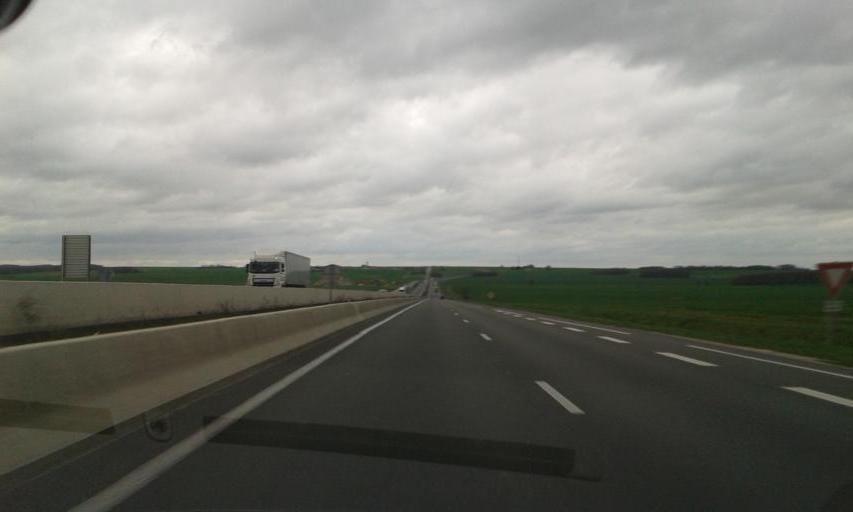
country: FR
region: Centre
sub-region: Departement d'Eure-et-Loir
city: Leves
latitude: 48.5098
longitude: 1.4625
